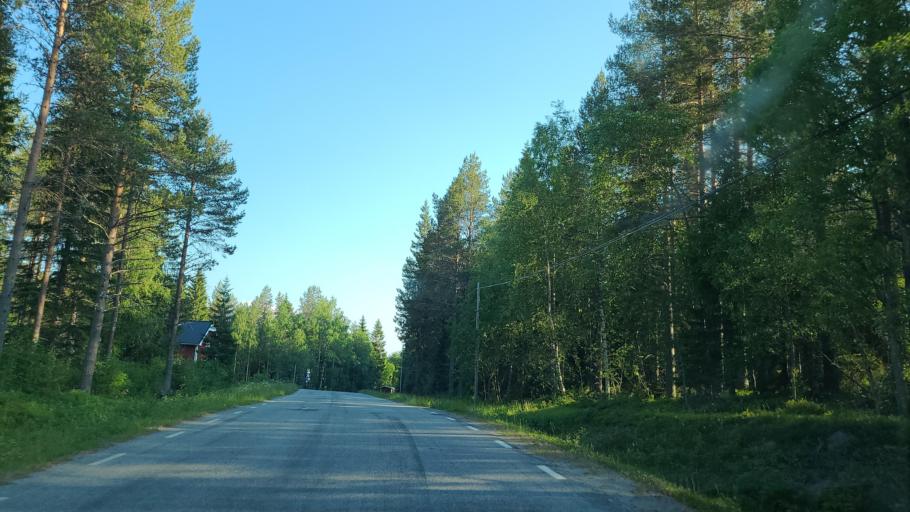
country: SE
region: Vaesterbotten
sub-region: Skelleftea Kommun
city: Burea
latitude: 64.3539
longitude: 21.3363
